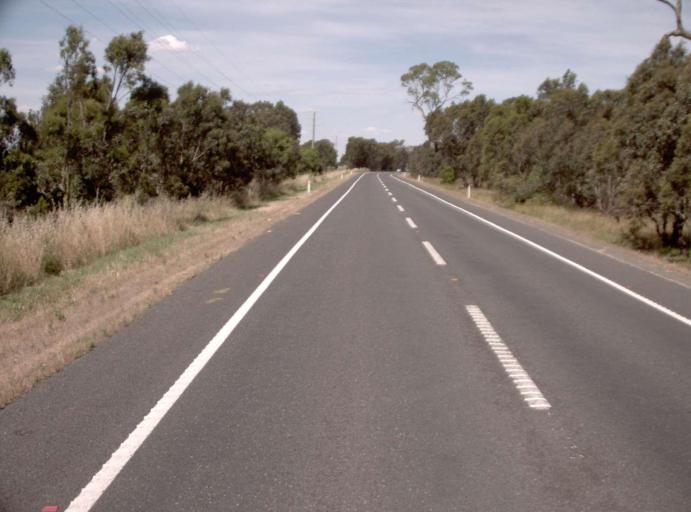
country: AU
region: Victoria
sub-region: East Gippsland
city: Bairnsdale
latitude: -37.8509
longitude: 147.5513
